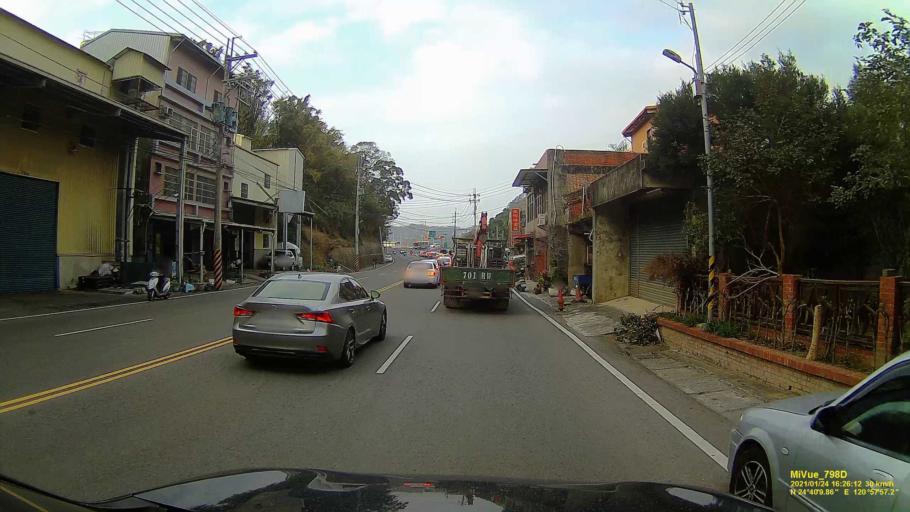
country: TW
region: Taiwan
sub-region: Hsinchu
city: Hsinchu
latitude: 24.6696
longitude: 120.9659
